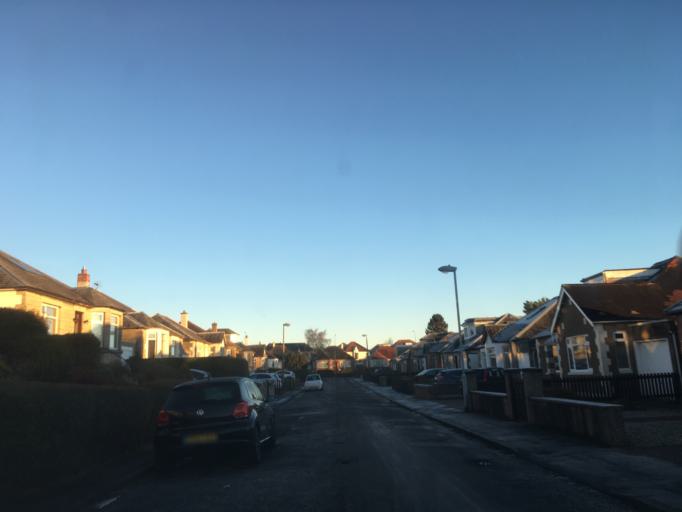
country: GB
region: Scotland
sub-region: Edinburgh
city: Currie
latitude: 55.9456
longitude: -3.2976
